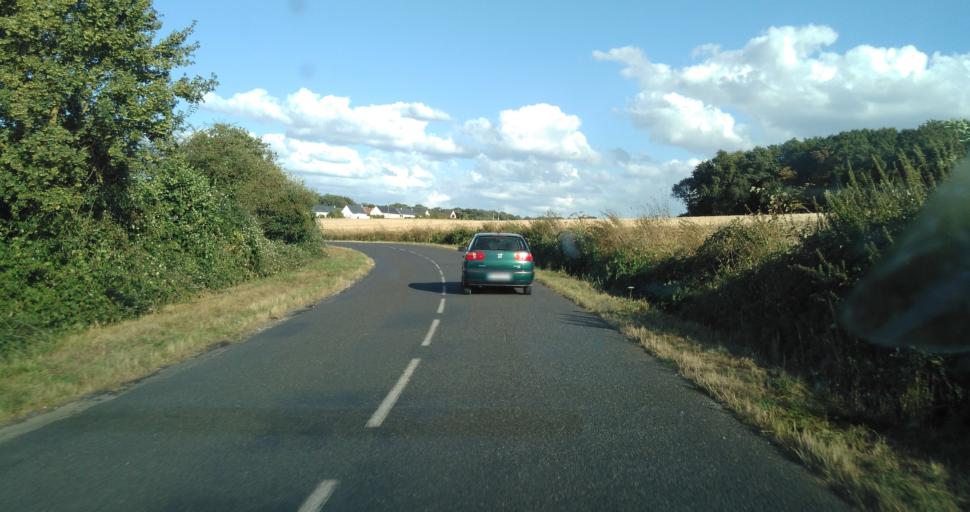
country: FR
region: Centre
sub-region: Departement d'Indre-et-Loire
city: Charge
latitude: 47.4072
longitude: 1.0403
